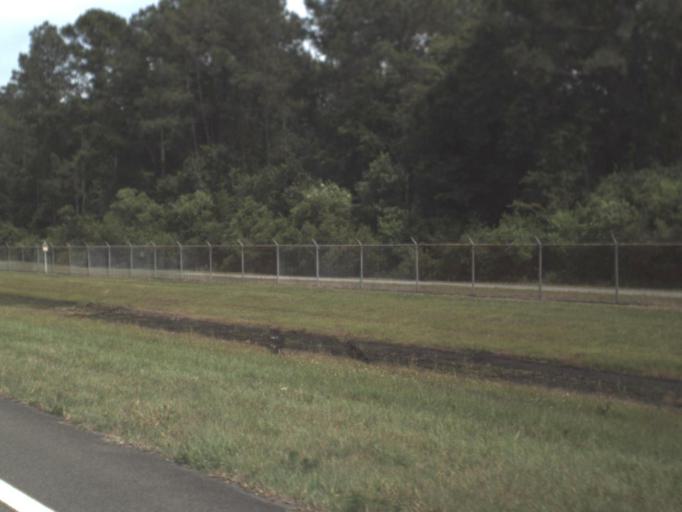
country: US
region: Florida
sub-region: Clay County
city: Bellair-Meadowbrook Terrace
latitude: 30.2467
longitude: -81.8534
